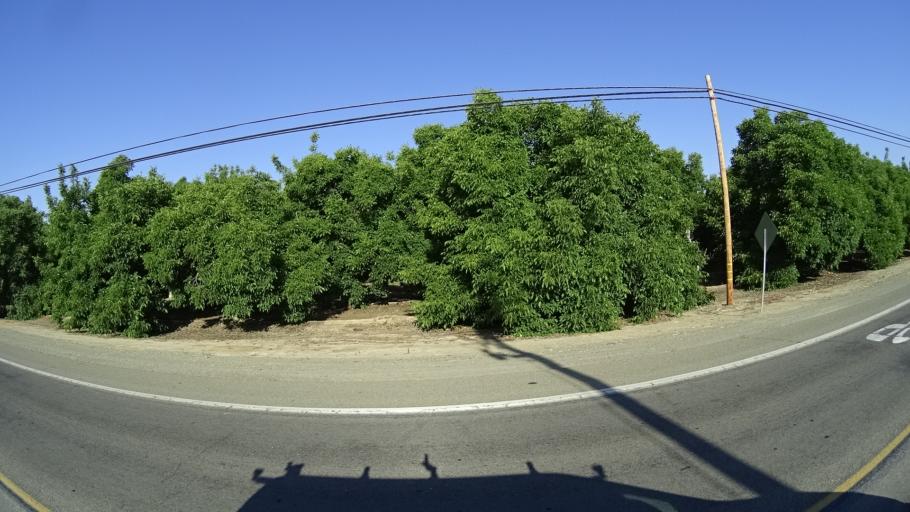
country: US
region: California
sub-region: Kings County
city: Armona
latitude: 36.2998
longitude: -119.7092
